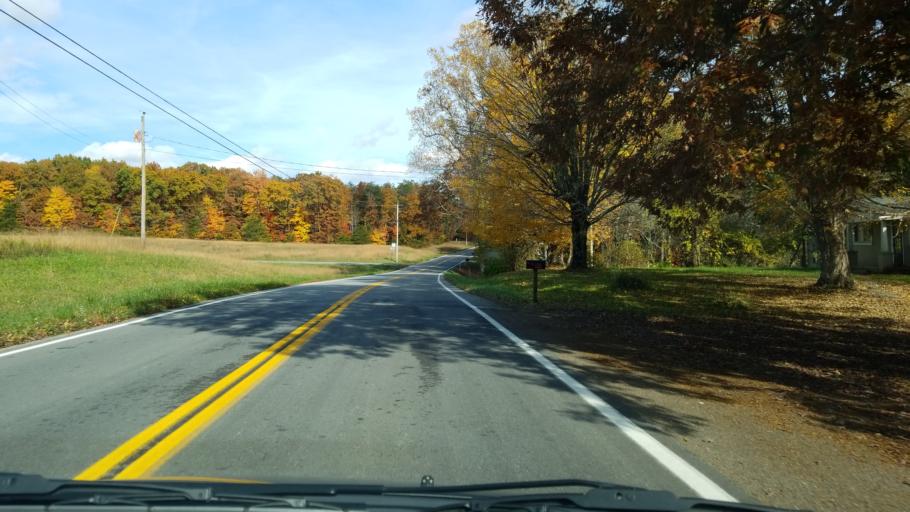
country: US
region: Tennessee
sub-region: Sequatchie County
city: Dunlap
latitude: 35.4655
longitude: -85.4800
